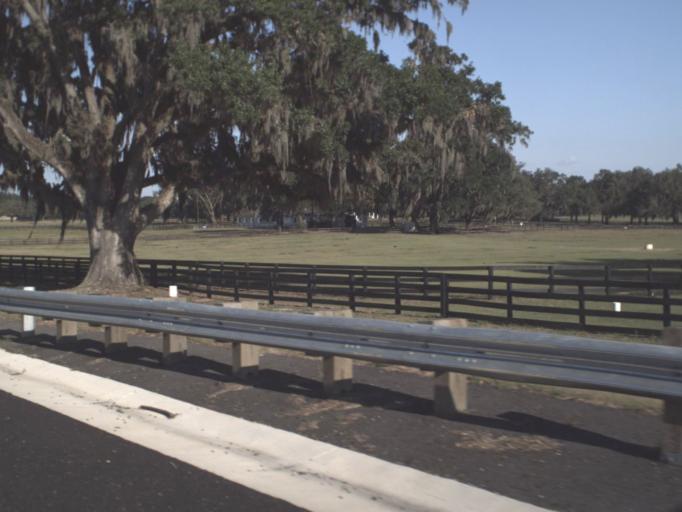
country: US
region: Florida
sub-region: Marion County
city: Ocala
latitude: 29.1866
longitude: -82.2598
